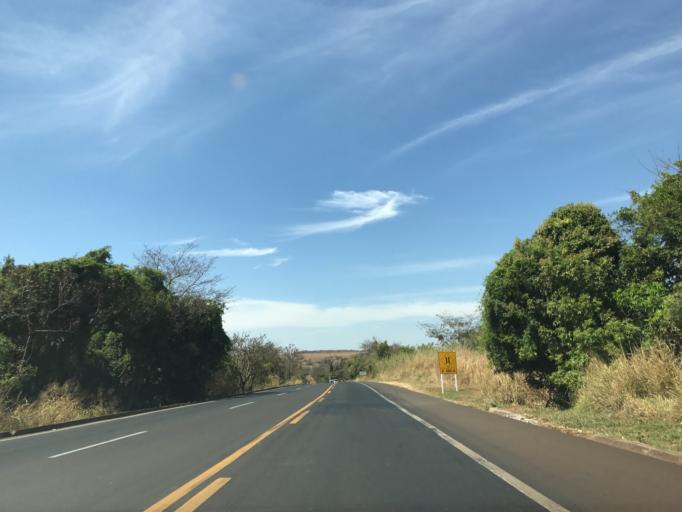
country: BR
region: Minas Gerais
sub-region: Monte Alegre De Minas
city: Monte Alegre de Minas
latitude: -18.9347
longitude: -49.0300
